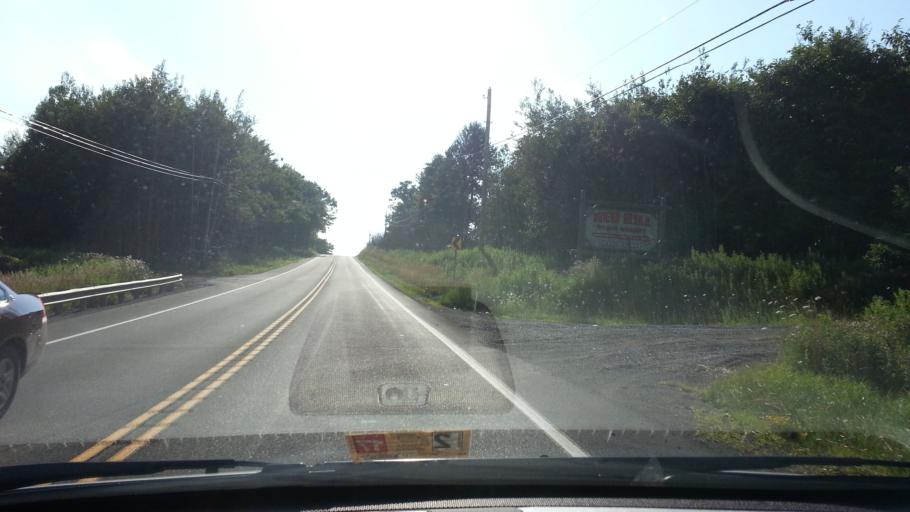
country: US
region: Pennsylvania
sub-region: Elk County
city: Saint Marys
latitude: 41.3520
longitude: -78.5289
